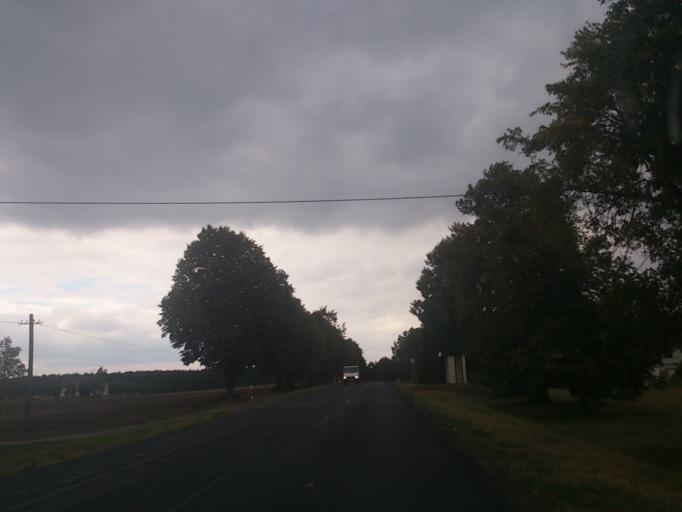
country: PL
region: Kujawsko-Pomorskie
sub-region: Powiat golubsko-dobrzynski
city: Golub-Dobrzyn
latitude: 53.0725
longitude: 19.0658
